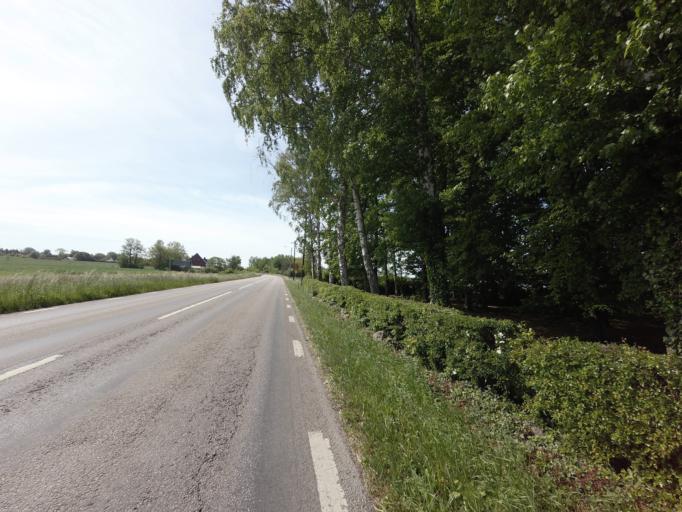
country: SE
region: Skane
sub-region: Helsingborg
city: Odakra
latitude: 56.1502
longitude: 12.6783
